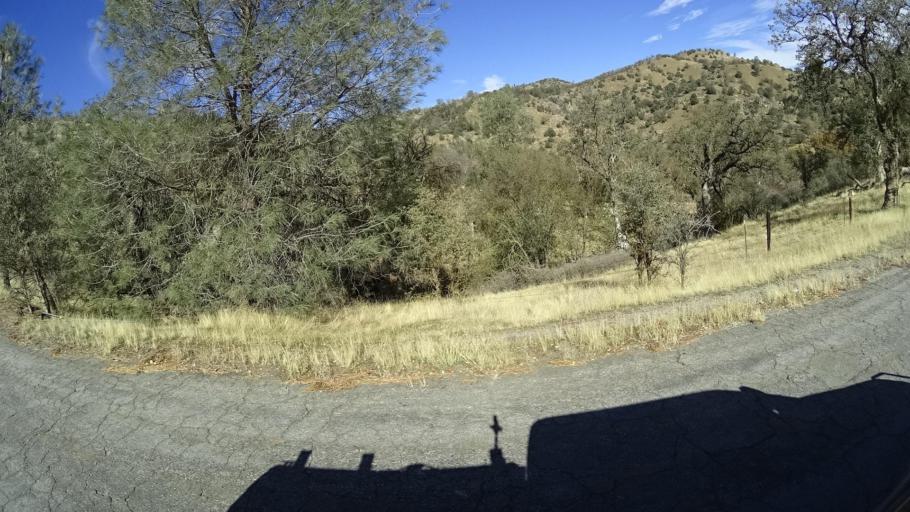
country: US
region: California
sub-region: Kern County
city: Alta Sierra
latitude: 35.6282
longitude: -118.7571
